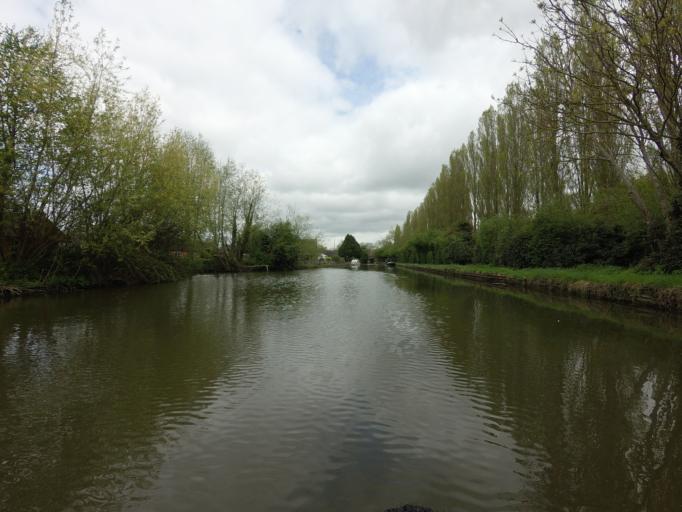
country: GB
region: England
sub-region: Milton Keynes
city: Water Eaton
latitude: 51.9867
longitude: -0.7177
